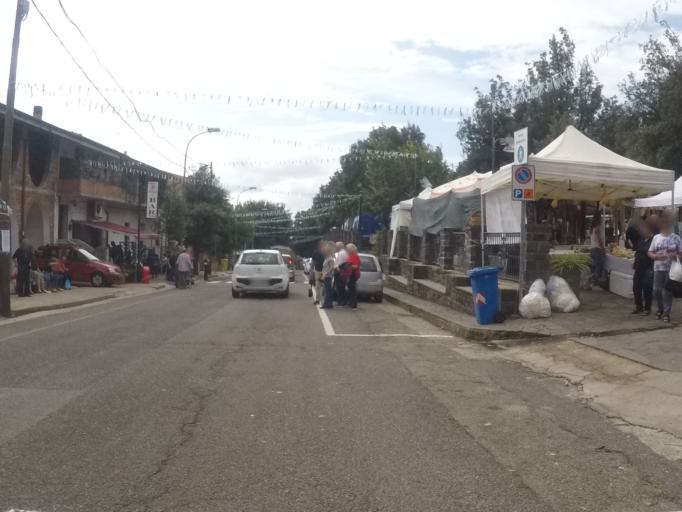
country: IT
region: Sardinia
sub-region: Provincia di Oristano
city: Bonarcado
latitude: 40.1006
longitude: 8.6546
